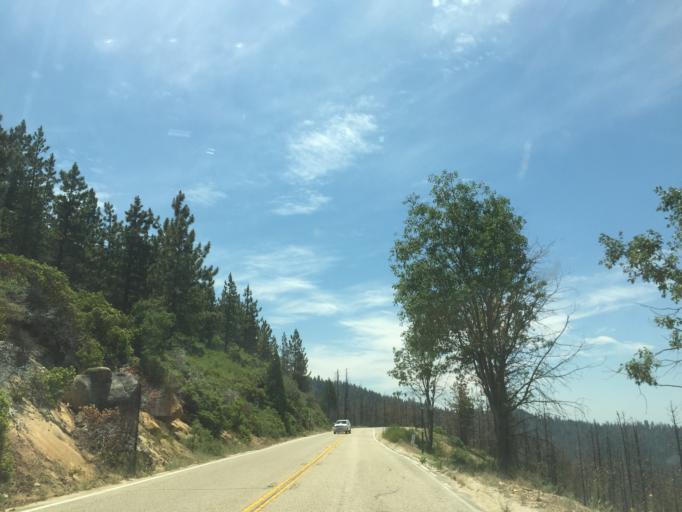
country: US
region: California
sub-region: Fresno County
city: Squaw Valley
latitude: 36.7743
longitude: -118.9612
